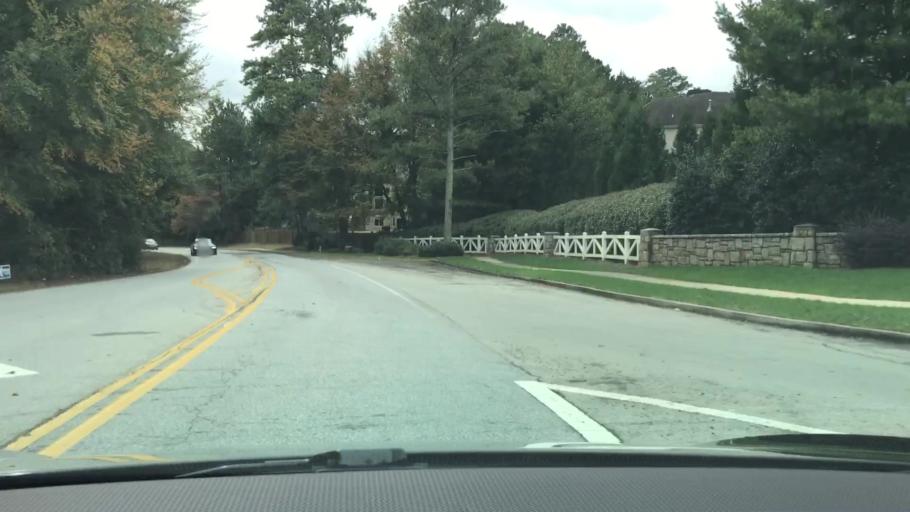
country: US
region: Georgia
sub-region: Gwinnett County
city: Suwanee
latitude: 34.0615
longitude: -84.0940
